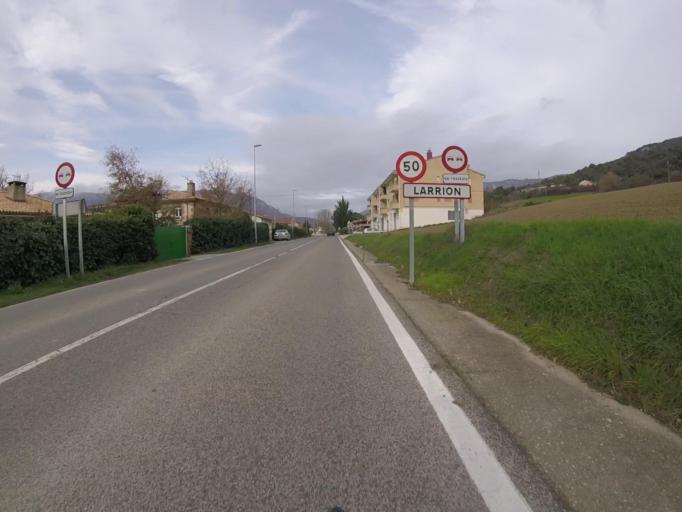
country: ES
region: Navarre
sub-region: Provincia de Navarra
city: Estella
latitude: 42.7090
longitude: -2.0702
